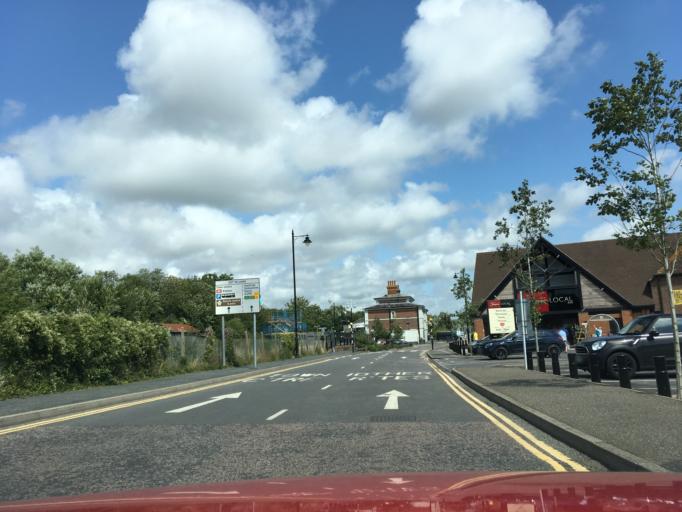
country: GB
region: England
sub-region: East Sussex
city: Rye
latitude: 50.9517
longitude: 0.7297
